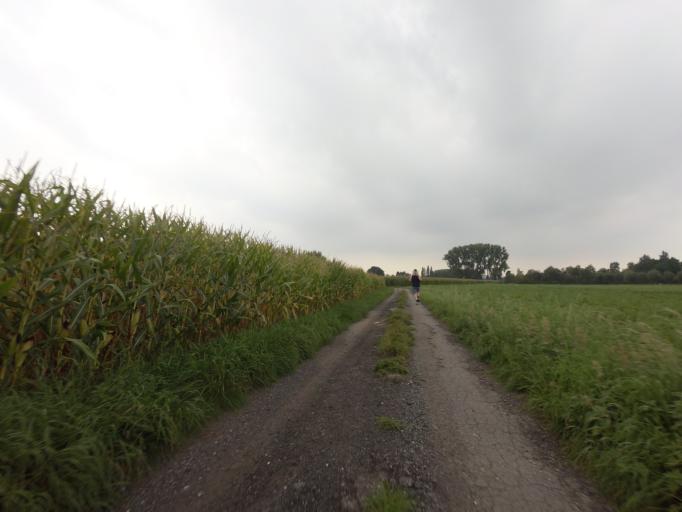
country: BE
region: Flanders
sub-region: Provincie Vlaams-Brabant
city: Boortmeerbeek
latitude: 50.9714
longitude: 4.5780
